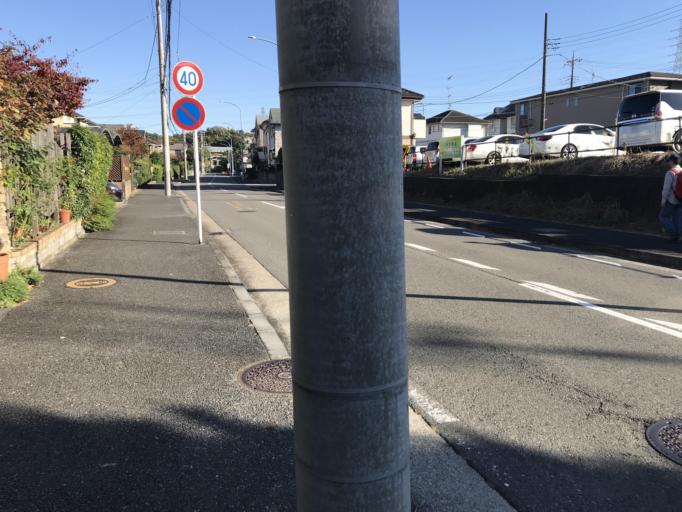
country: JP
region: Tokyo
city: Chofugaoka
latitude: 35.5647
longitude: 139.6063
